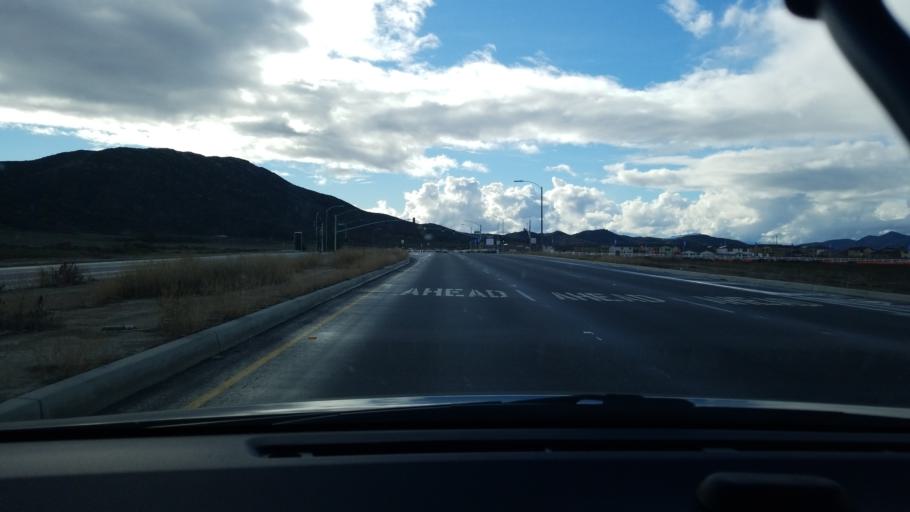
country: US
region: California
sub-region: Riverside County
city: Winchester
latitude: 33.6951
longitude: -117.0910
